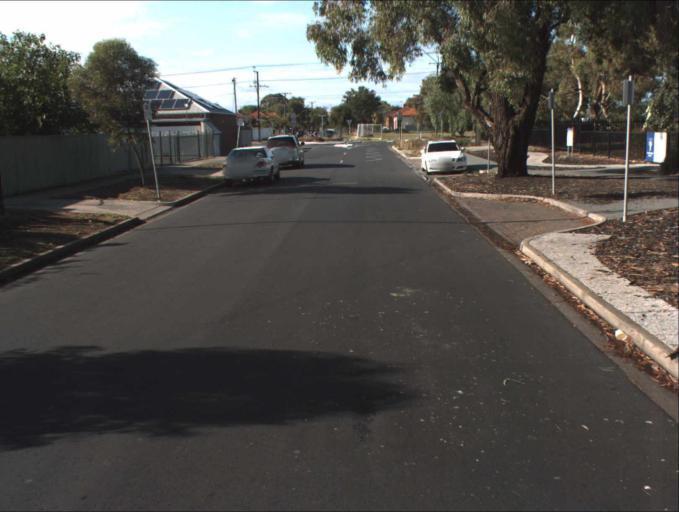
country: AU
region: South Australia
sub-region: Charles Sturt
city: Woodville North
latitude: -34.8632
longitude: 138.5521
